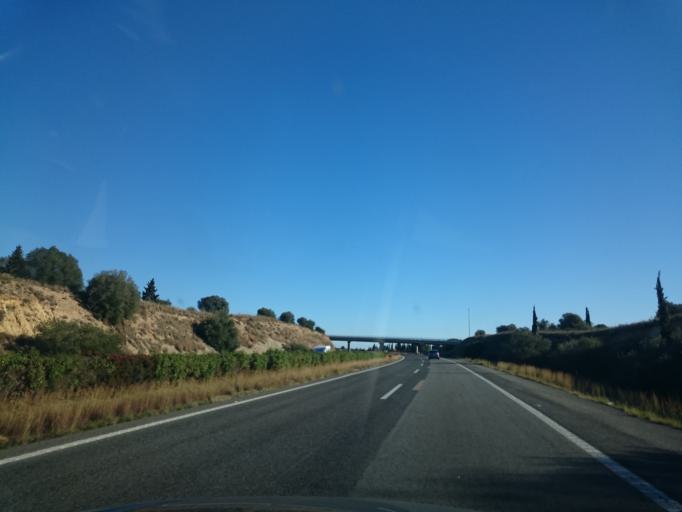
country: ES
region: Catalonia
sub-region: Provincia de Tarragona
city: Amposta
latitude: 40.7311
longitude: 0.5823
